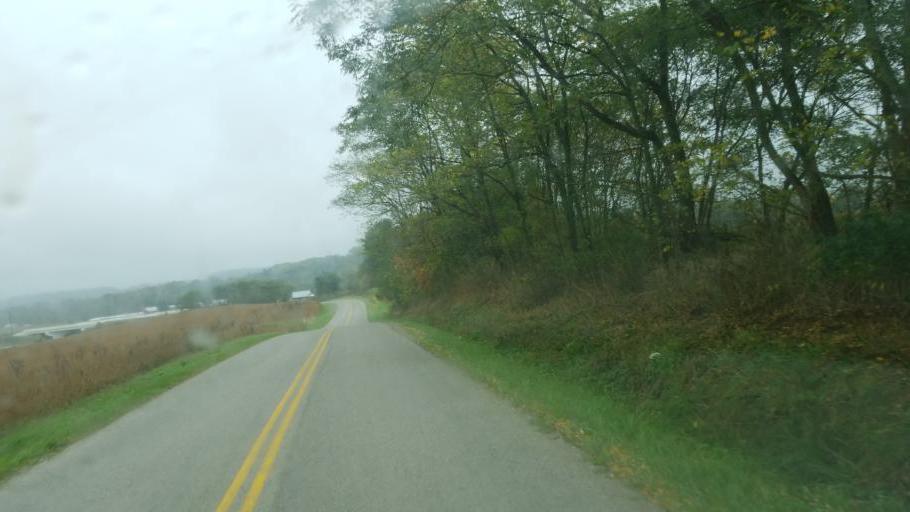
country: US
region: Ohio
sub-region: Richland County
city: Lexington
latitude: 40.6009
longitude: -82.5901
